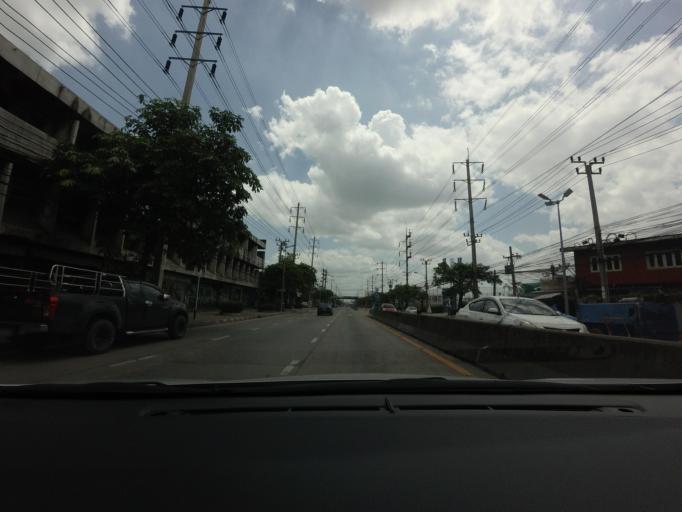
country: TH
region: Samut Prakan
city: Phra Pradaeng
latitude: 13.6488
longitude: 100.5647
